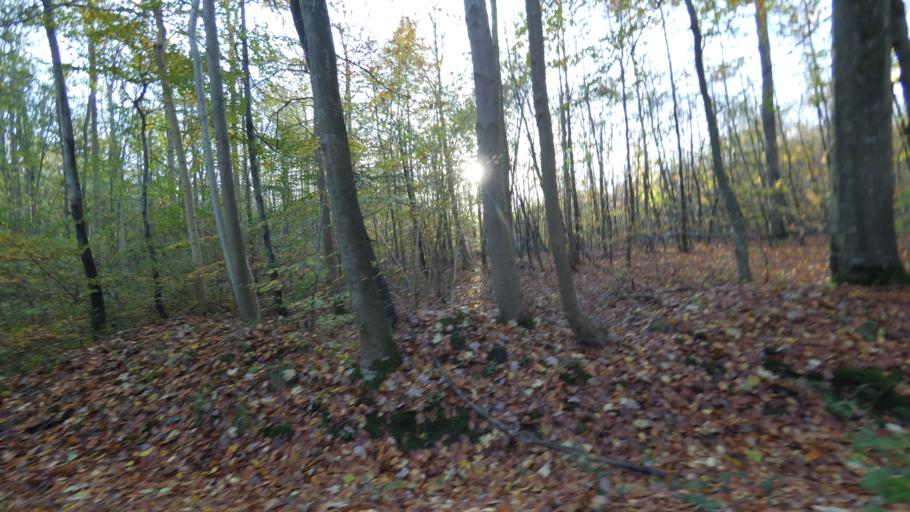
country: DK
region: Central Jutland
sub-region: Odder Kommune
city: Odder
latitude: 55.9041
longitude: 10.2273
